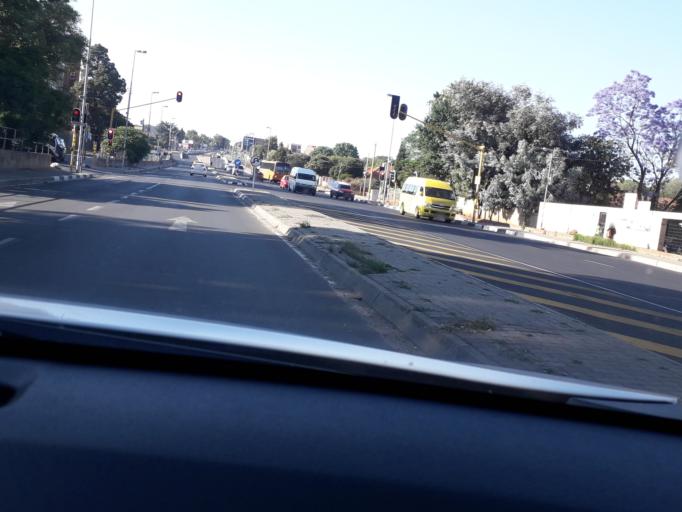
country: ZA
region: Gauteng
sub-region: City of Johannesburg Metropolitan Municipality
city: Johannesburg
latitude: -26.1342
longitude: 28.0856
